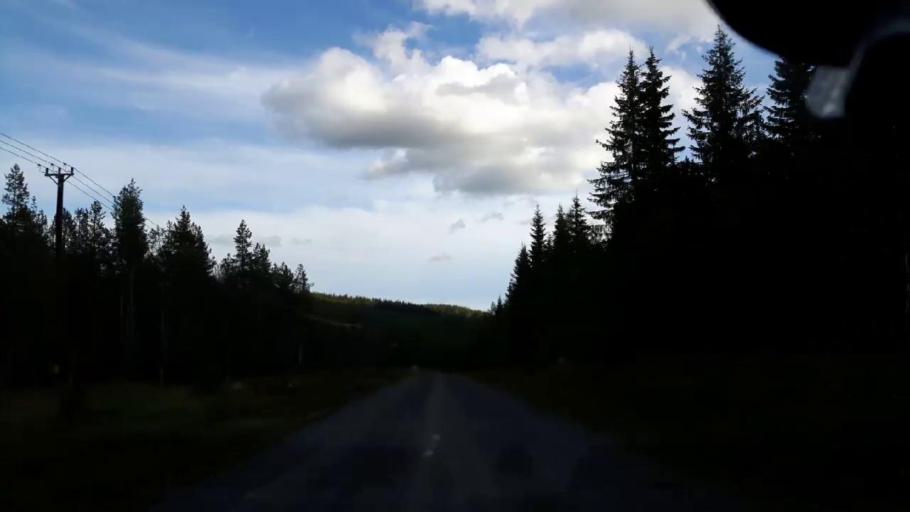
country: SE
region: Jaemtland
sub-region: Ragunda Kommun
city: Hammarstrand
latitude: 63.4238
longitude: 16.0617
